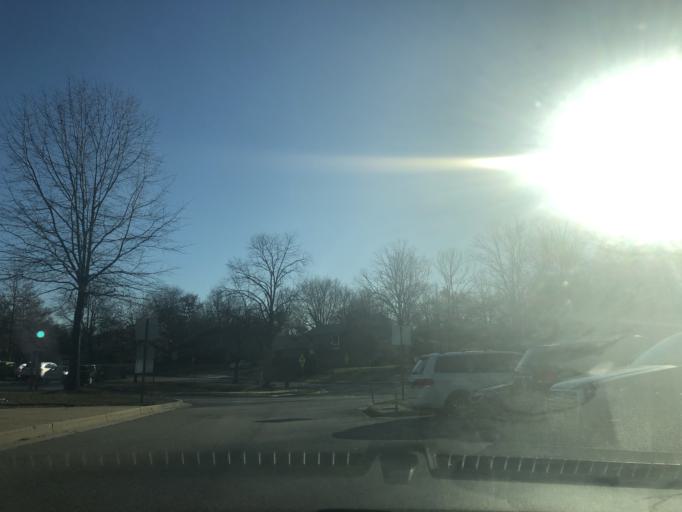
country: US
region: Maryland
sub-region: Howard County
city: Columbia
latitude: 39.2077
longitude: -76.8399
